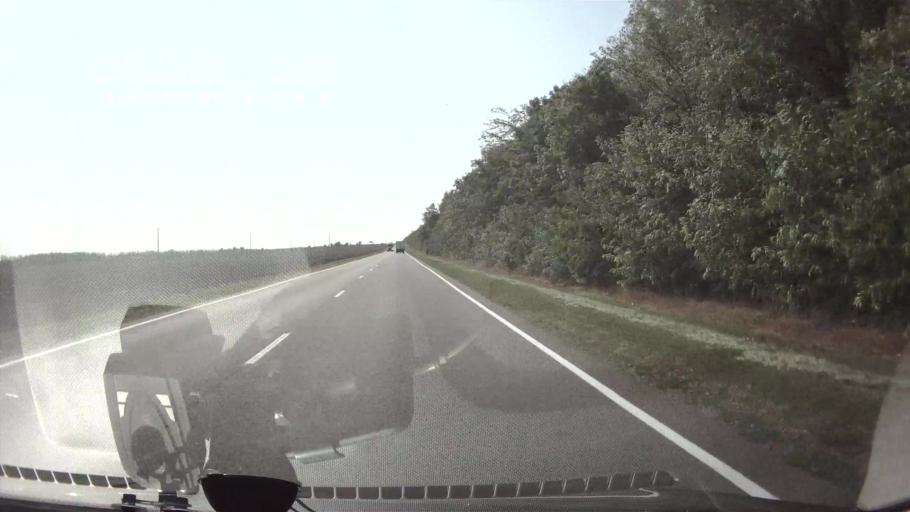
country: RU
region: Krasnodarskiy
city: Novopokrovskaya
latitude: 45.8897
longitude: 40.7209
